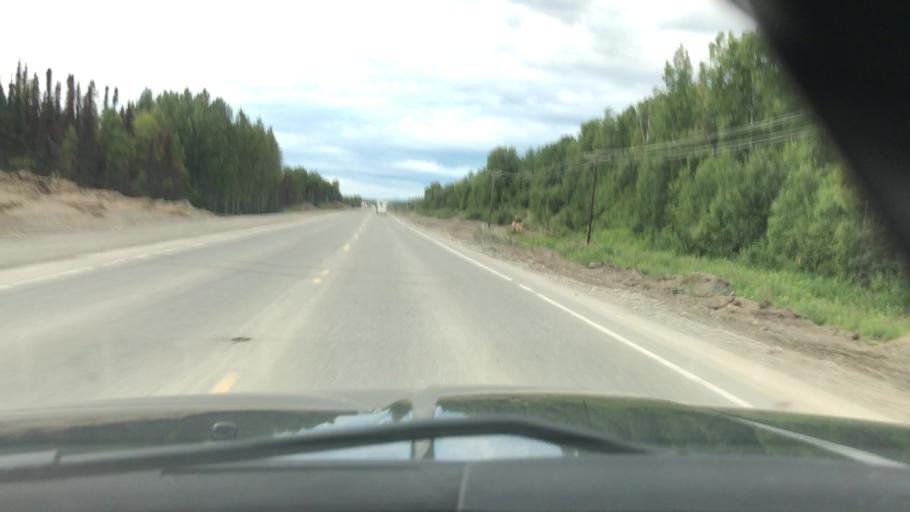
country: US
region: Alaska
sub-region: Matanuska-Susitna Borough
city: Y
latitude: 62.1142
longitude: -150.0517
